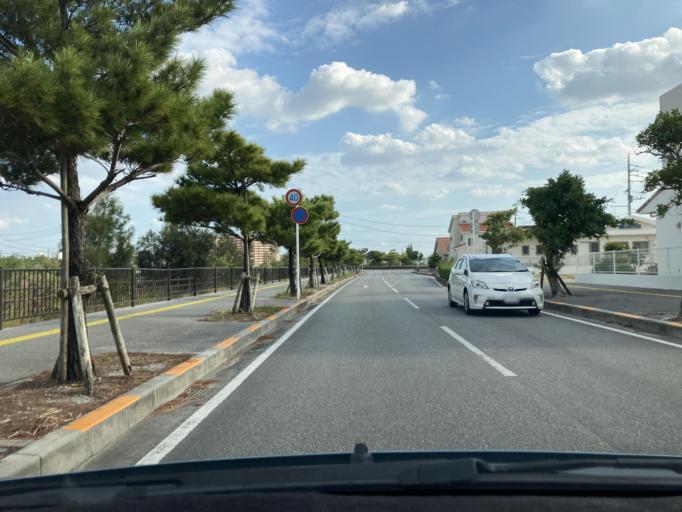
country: JP
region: Okinawa
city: Itoman
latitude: 26.1552
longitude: 127.6666
